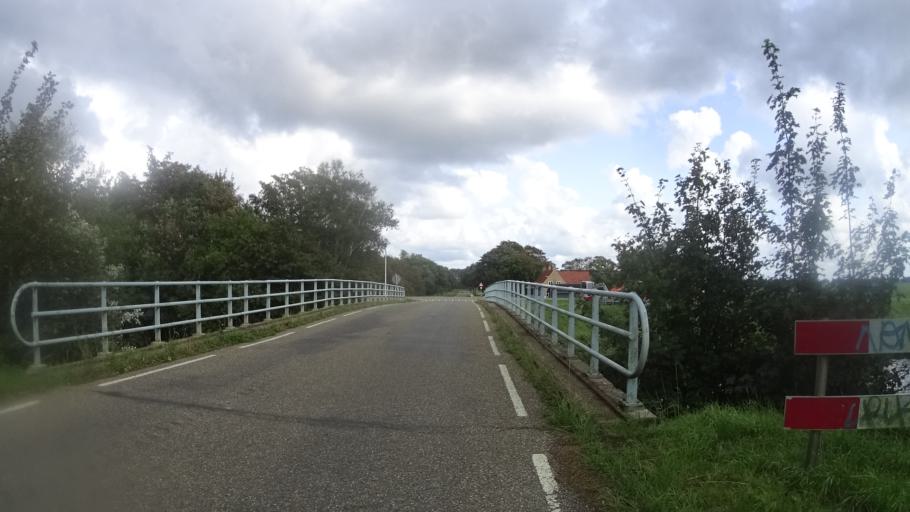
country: NL
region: North Holland
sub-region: Gemeente Hollands Kroon
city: Den Oever
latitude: 52.8979
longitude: 5.0147
